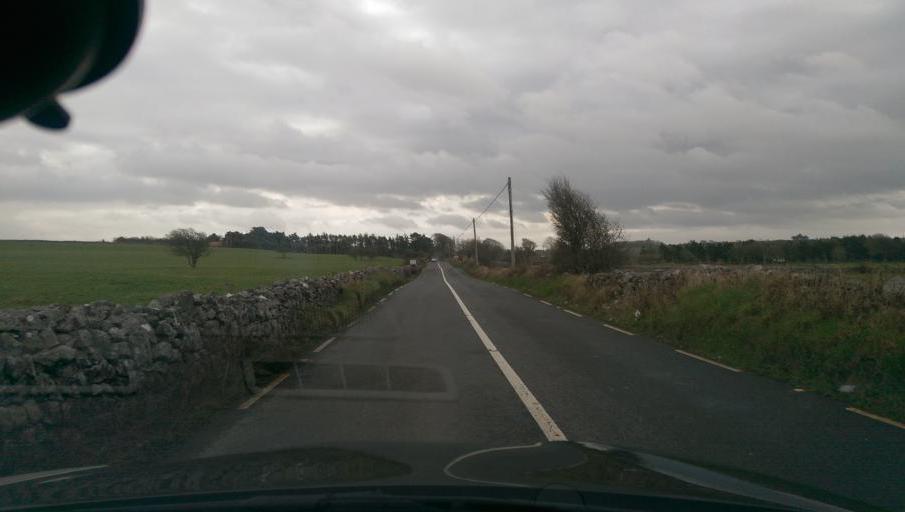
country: IE
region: Connaught
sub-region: County Galway
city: Athenry
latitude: 53.3250
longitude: -8.8376
